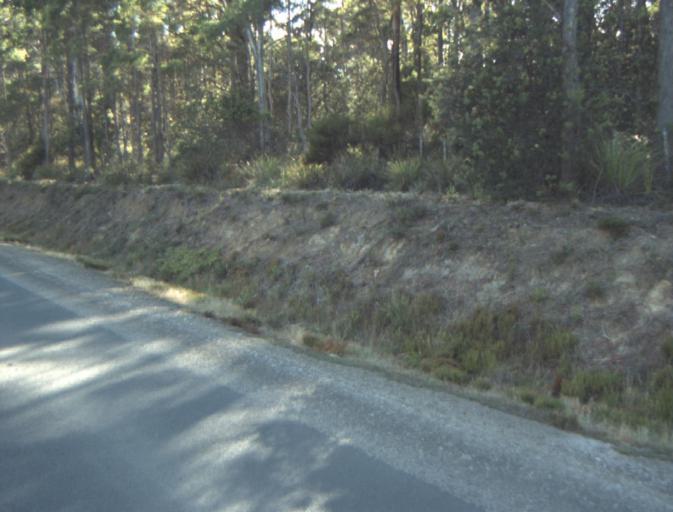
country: AU
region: Tasmania
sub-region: Launceston
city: Mayfield
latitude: -41.3198
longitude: 147.1894
